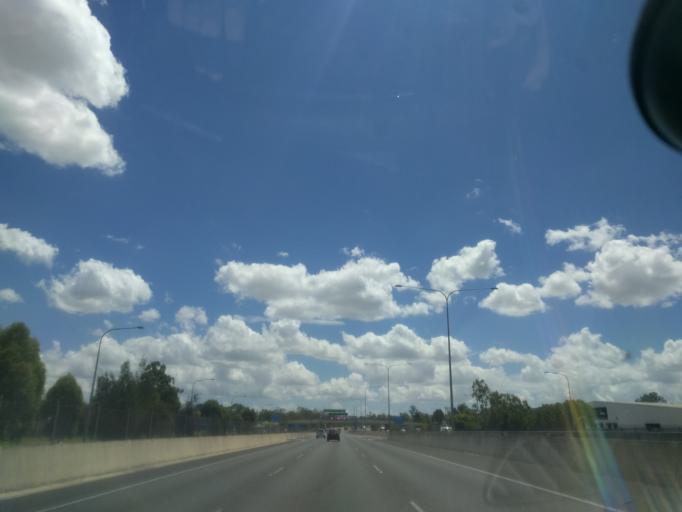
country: AU
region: Queensland
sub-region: Brisbane
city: Wacol
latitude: -27.5912
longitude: 152.9250
